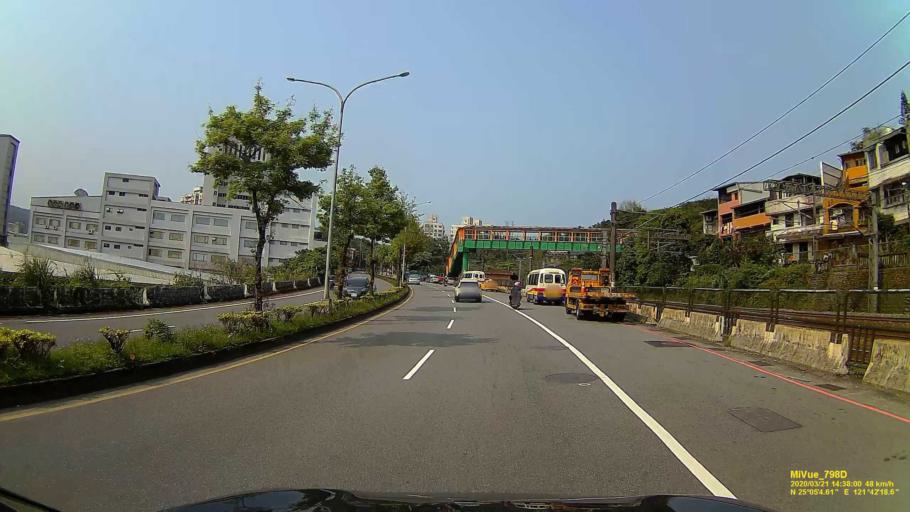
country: TW
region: Taiwan
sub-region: Keelung
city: Keelung
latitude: 25.0848
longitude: 121.7052
